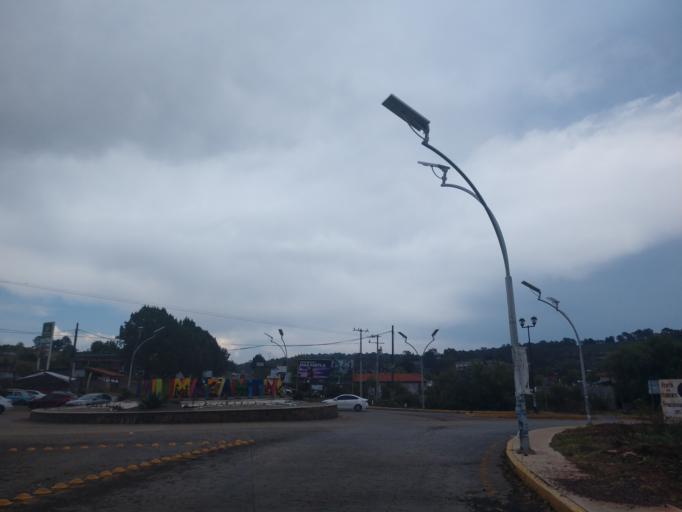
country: MX
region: Jalisco
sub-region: Mazamitla
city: Mazamitla
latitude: 19.9323
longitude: -103.0391
